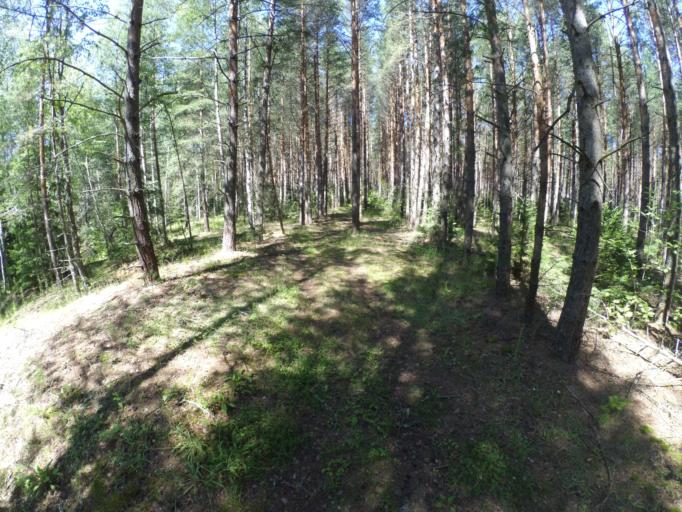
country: RU
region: Moskovskaya
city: Fosforitnyy
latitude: 55.3411
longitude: 38.9224
